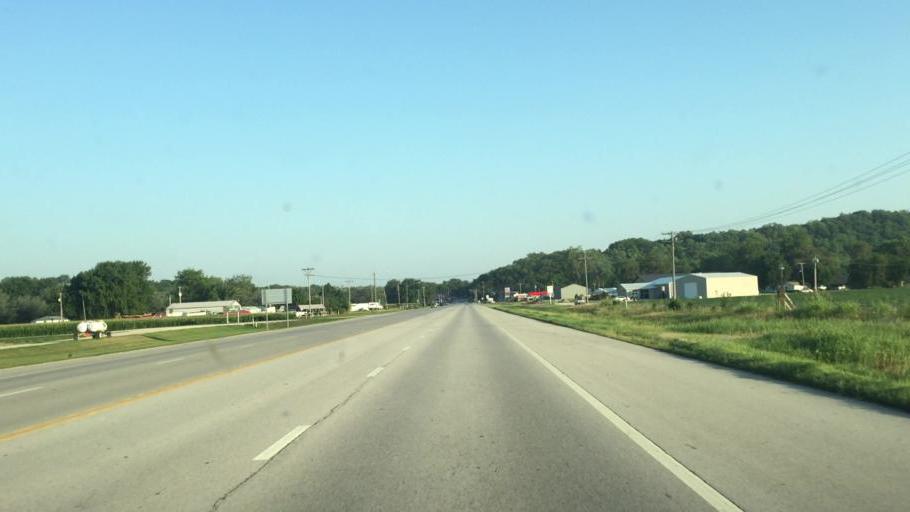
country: US
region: Kansas
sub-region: Doniphan County
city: Wathena
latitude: 39.7558
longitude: -94.9384
